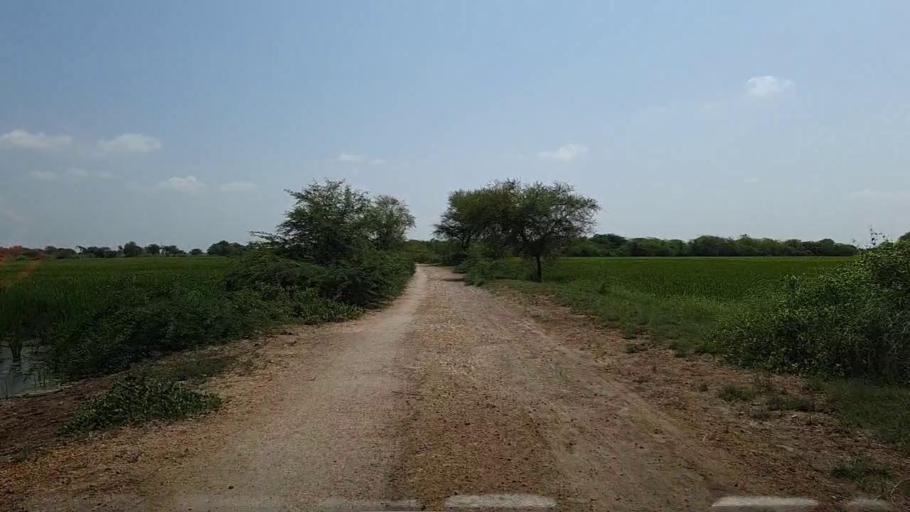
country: PK
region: Sindh
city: Kario
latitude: 24.6989
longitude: 68.6156
